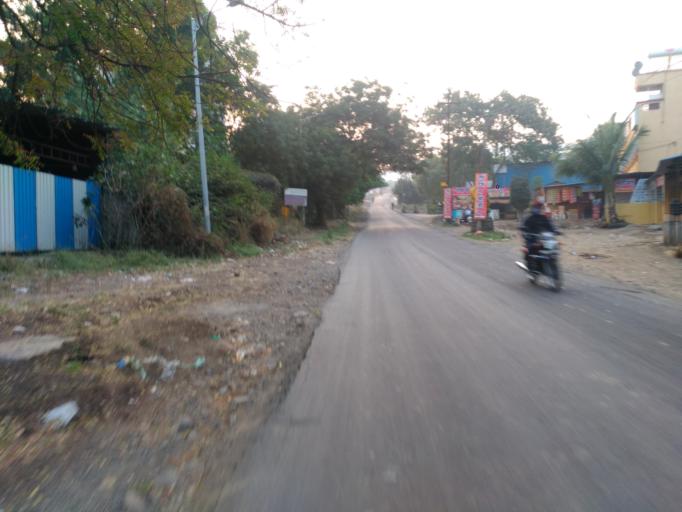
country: IN
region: Maharashtra
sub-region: Pune Division
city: Pune
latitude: 18.4288
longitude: 73.8994
